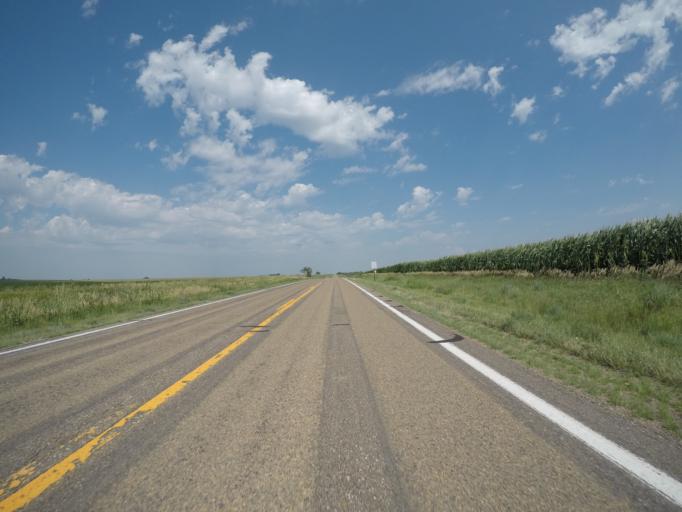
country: US
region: Nebraska
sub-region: Nuckolls County
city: Superior
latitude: 40.0166
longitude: -97.8444
